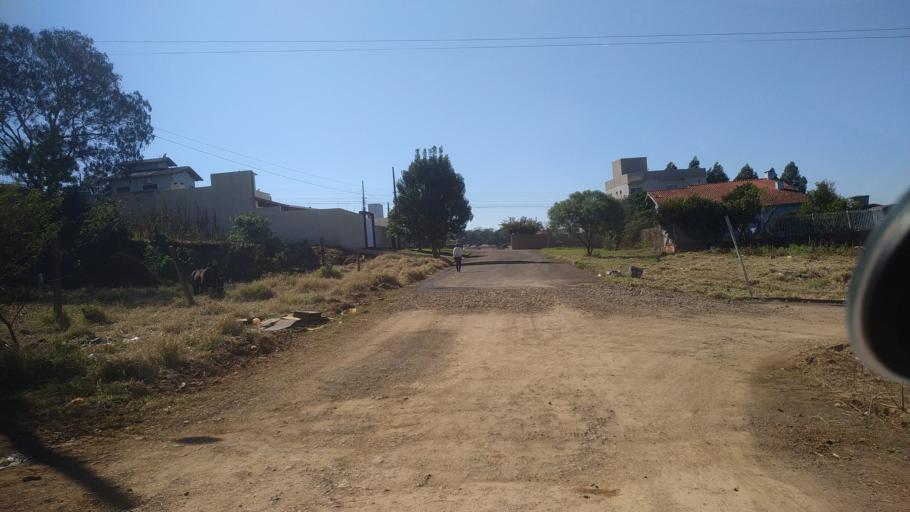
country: BR
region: Santa Catarina
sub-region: Chapeco
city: Chapeco
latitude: -27.0920
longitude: -52.5957
